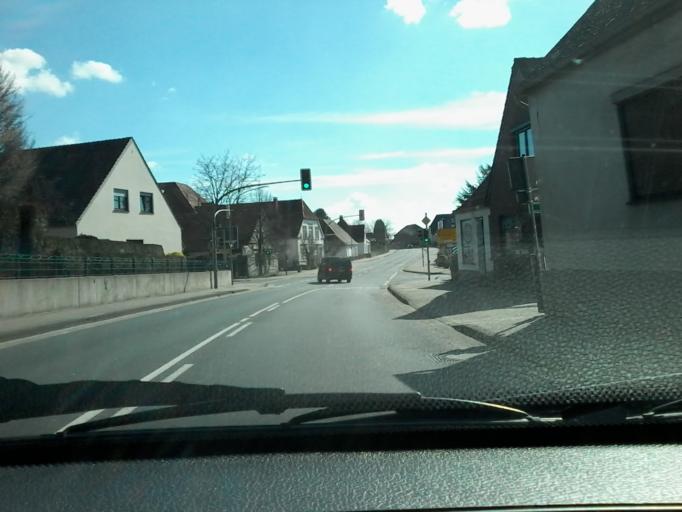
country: DE
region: Lower Saxony
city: Ahsen-Oetzen
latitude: 52.9955
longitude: 9.1152
